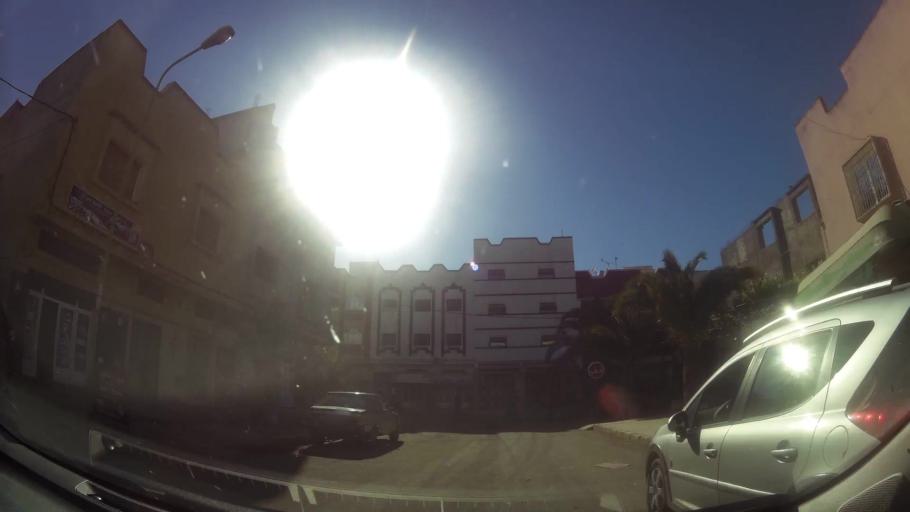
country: MA
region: Oriental
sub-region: Berkane-Taourirt
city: Ahfir
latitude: 34.9561
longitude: -2.1019
